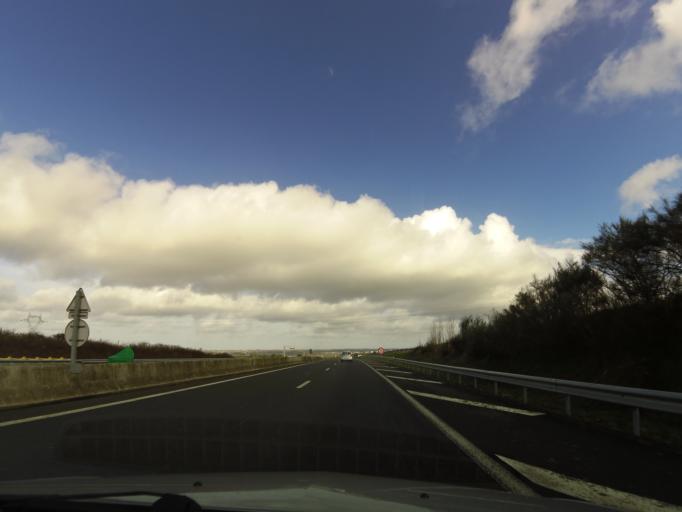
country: FR
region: Lower Normandy
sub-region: Departement de la Manche
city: Conde-sur-Vire
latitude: 49.0786
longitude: -1.0294
